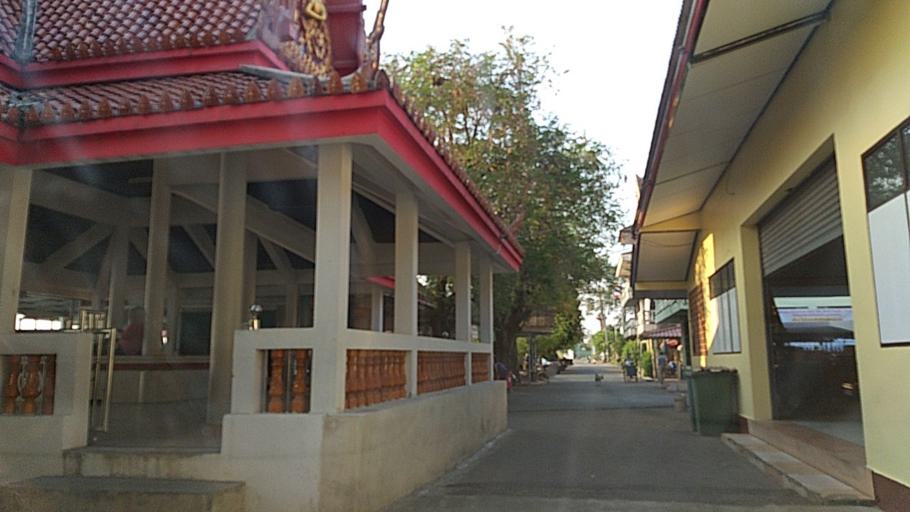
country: TH
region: Phra Nakhon Si Ayutthaya
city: Ban Bang Kadi Pathum Thani
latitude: 14.0036
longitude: 100.5409
